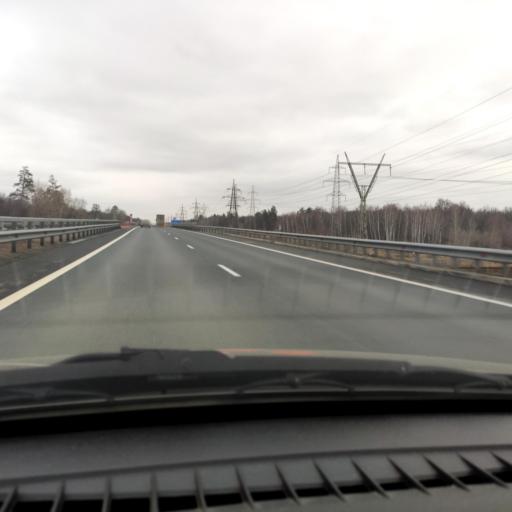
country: RU
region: Samara
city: Pribrezhnyy
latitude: 53.5176
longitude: 49.8330
